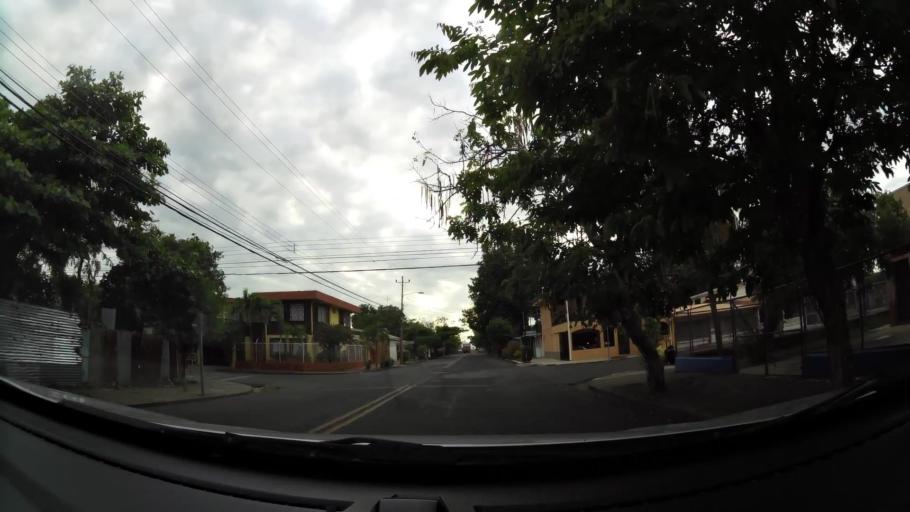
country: CR
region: Puntarenas
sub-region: Canton Central de Puntarenas
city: Puntarenas
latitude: 9.9761
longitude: -84.8467
